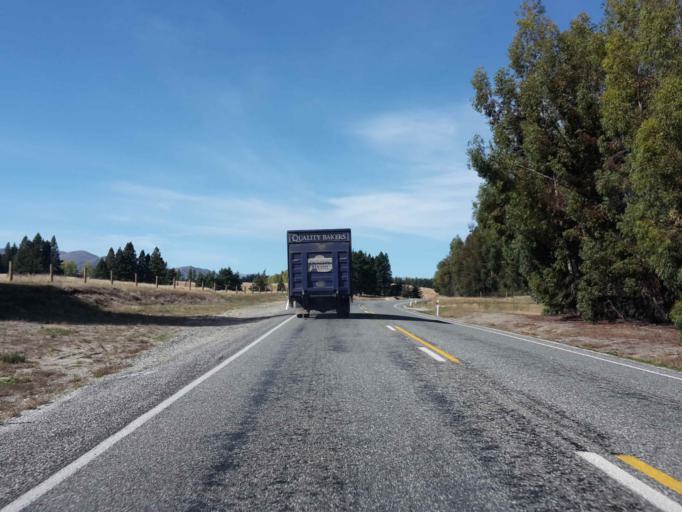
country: NZ
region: Otago
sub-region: Queenstown-Lakes District
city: Wanaka
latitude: -44.7076
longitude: 169.2029
